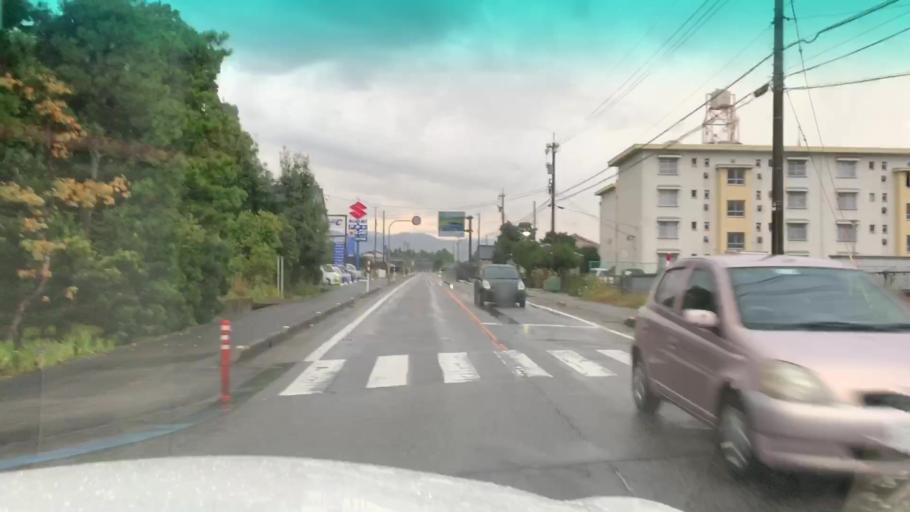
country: JP
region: Toyama
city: Kamiichi
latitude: 36.6671
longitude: 137.3276
